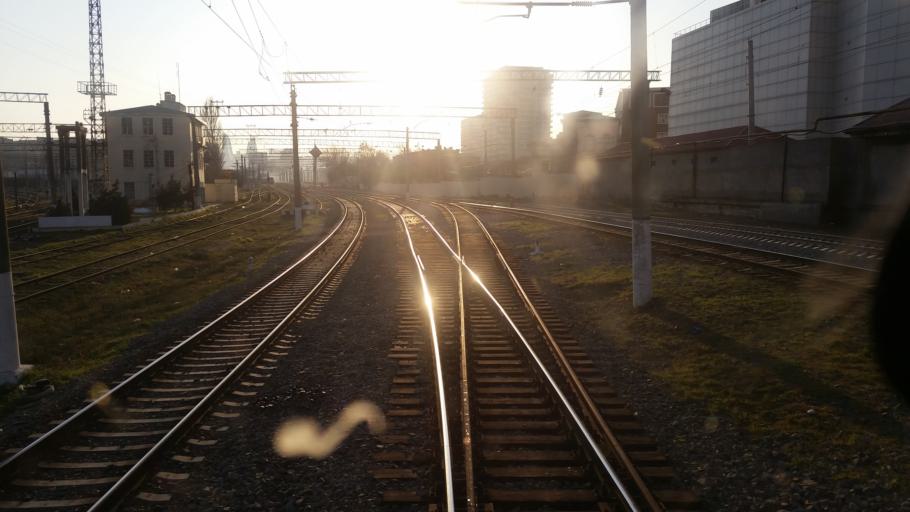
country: AZ
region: Baki
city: Baku
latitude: 40.3897
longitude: 49.8620
